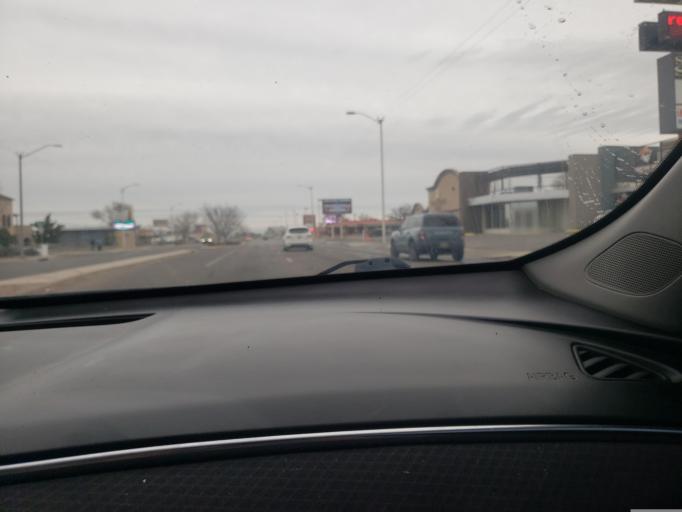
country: US
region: New Mexico
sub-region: Bernalillo County
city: North Valley
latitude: 35.1192
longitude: -106.5864
